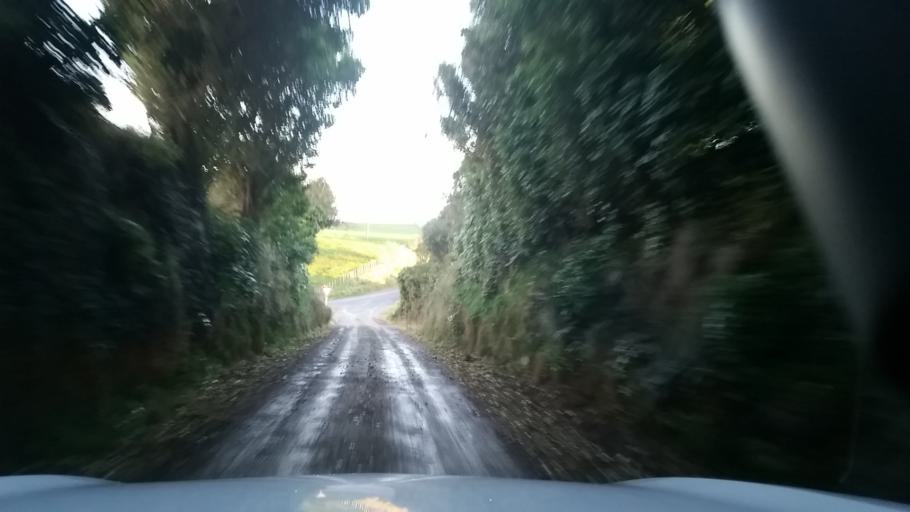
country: NZ
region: Manawatu-Wanganui
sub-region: Wanganui District
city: Wanganui
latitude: -39.8022
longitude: 174.8036
